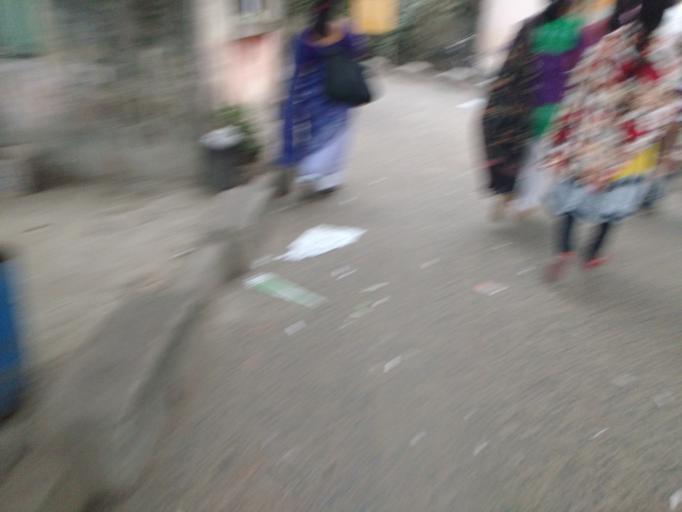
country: IN
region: West Bengal
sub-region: Haora
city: Chakapara
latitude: 22.6301
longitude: 88.3582
